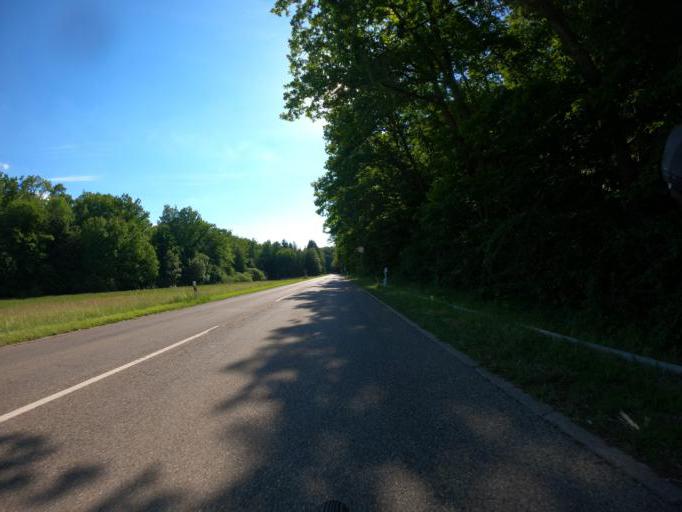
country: DE
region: Baden-Wuerttemberg
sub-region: Regierungsbezirk Stuttgart
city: Sindelfingen
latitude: 48.7468
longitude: 9.0239
